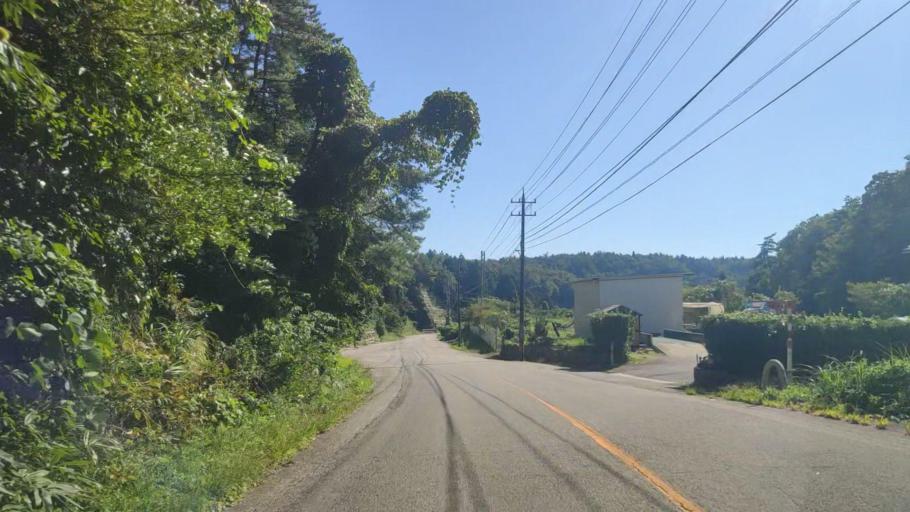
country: JP
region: Ishikawa
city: Nanao
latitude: 37.3184
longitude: 137.1651
